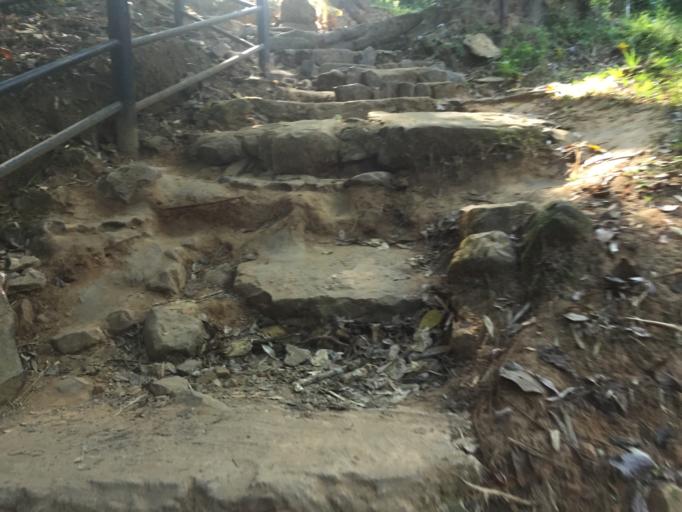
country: TH
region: Phetchabun
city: Khao Kho
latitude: 16.6294
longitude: 100.9394
